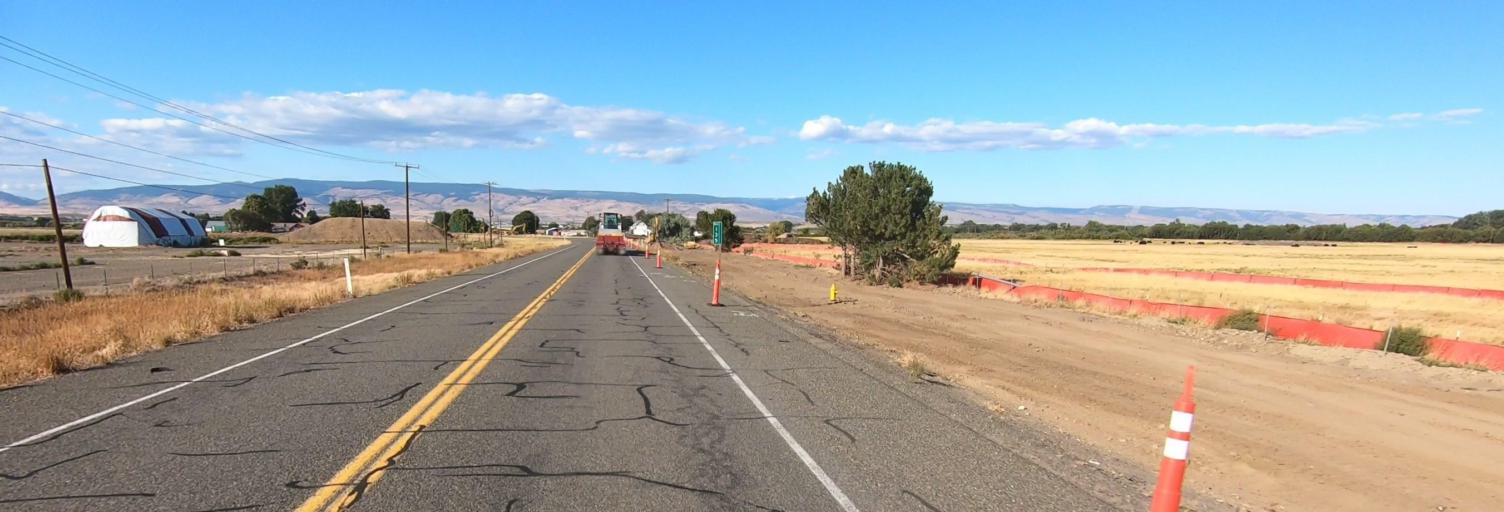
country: US
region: Washington
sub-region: Kittitas County
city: Ellensburg
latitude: 47.0154
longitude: -120.5925
